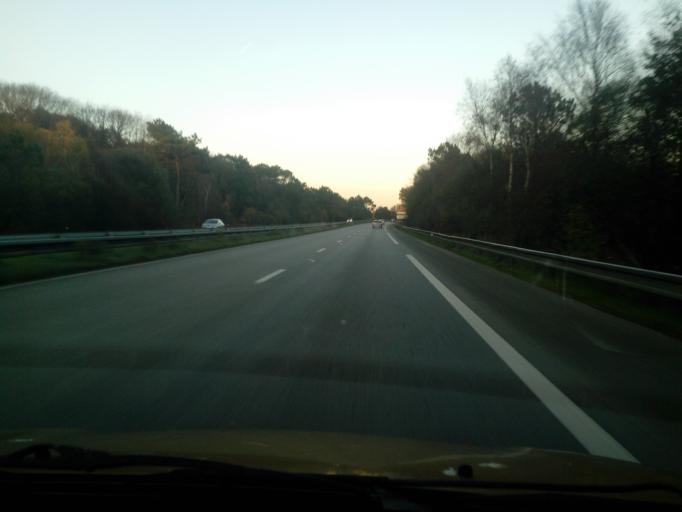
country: FR
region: Brittany
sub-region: Departement du Morbihan
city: Branderion
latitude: 47.8293
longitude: -3.1946
